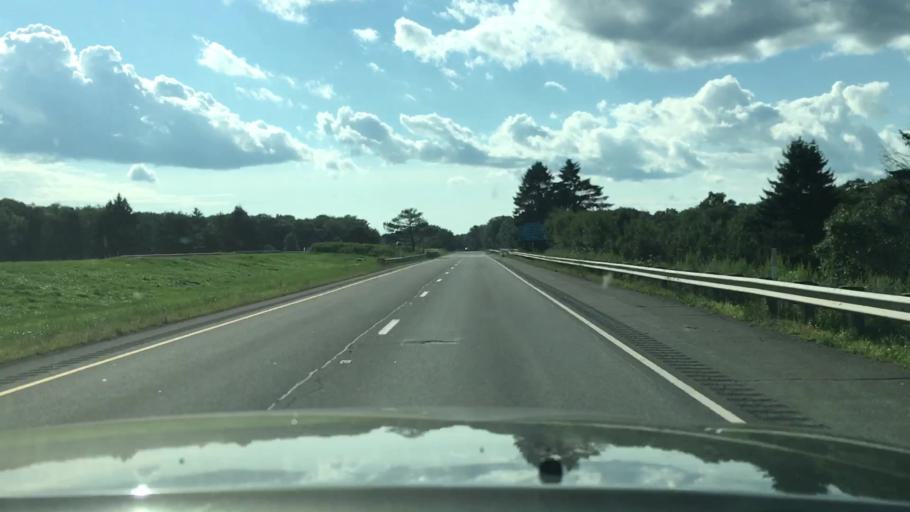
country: US
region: Pennsylvania
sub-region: Wayne County
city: Hawley
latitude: 41.3606
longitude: -75.2007
